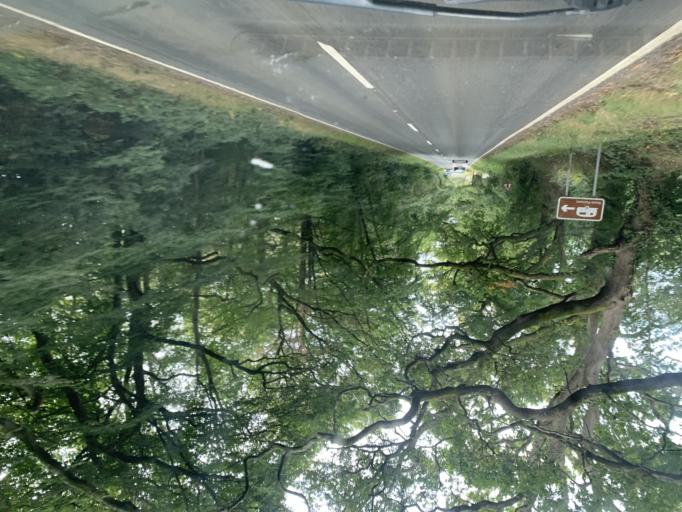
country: GB
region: England
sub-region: Hampshire
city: Cadnam
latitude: 50.9403
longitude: -1.5494
